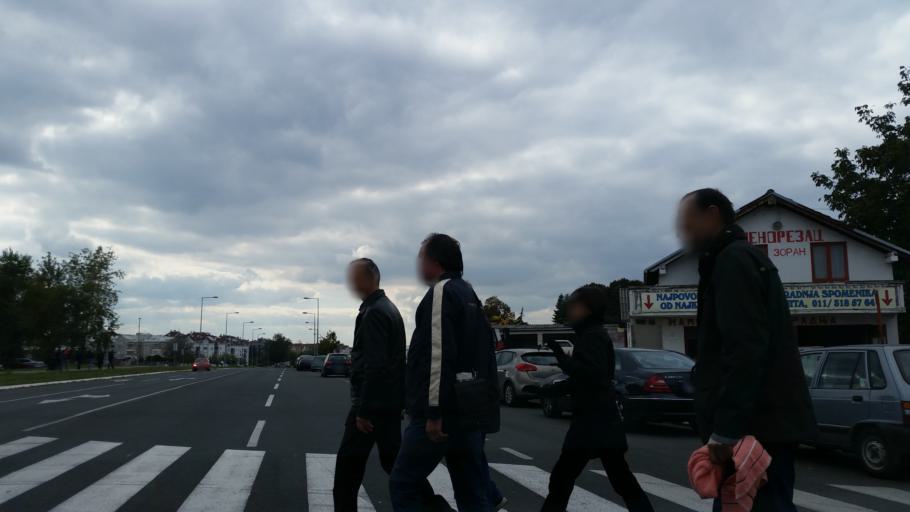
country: RS
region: Central Serbia
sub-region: Belgrade
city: Zemun
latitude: 44.8163
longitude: 20.3703
